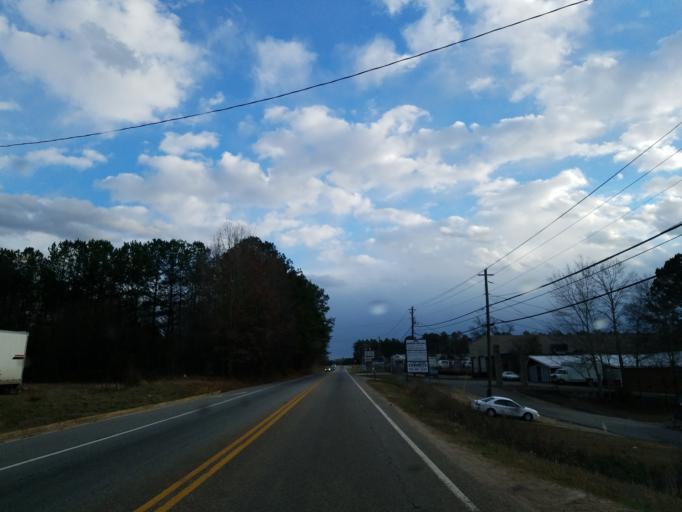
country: US
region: Georgia
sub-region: Henry County
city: Stockbridge
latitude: 33.5318
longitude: -84.1985
